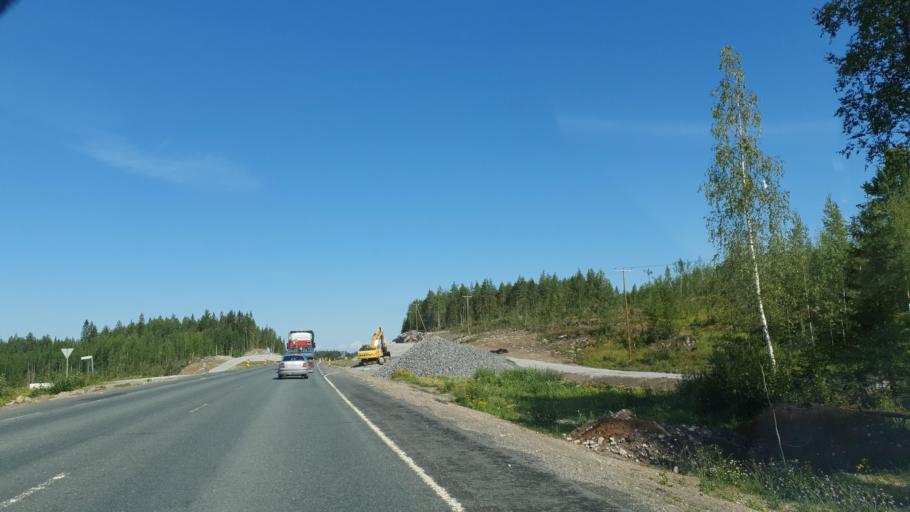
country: FI
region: Northern Savo
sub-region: Ylae-Savo
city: Lapinlahti
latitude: 63.2788
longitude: 27.4572
